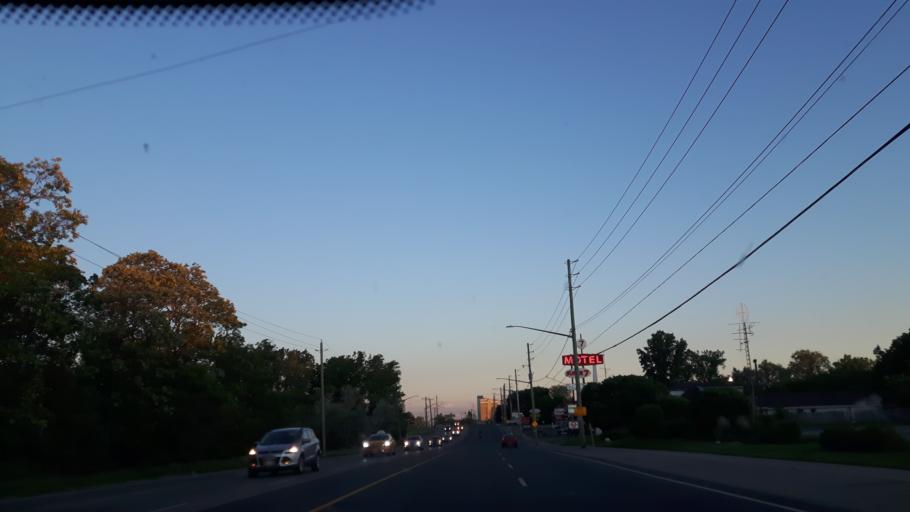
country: CA
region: Ontario
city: London
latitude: 42.9498
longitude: -81.2283
